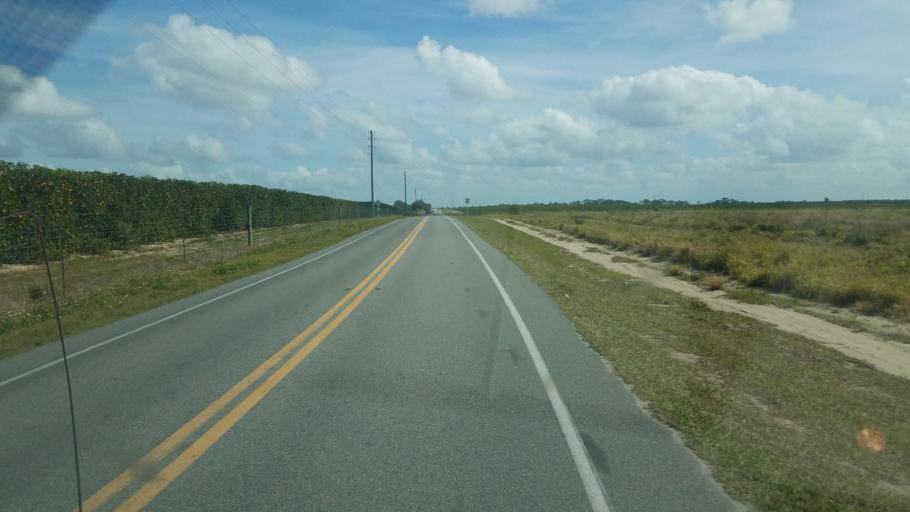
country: US
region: Florida
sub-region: Polk County
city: Babson Park
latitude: 27.9252
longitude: -81.4835
